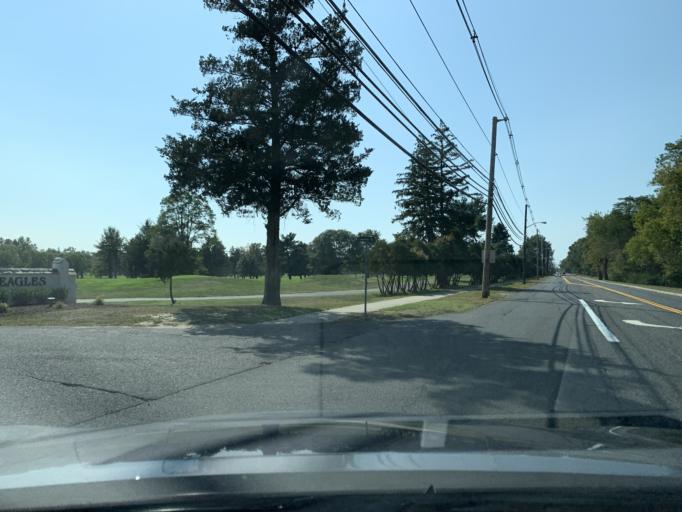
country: US
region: New Jersey
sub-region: Monmouth County
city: Eatontown
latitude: 40.3044
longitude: -74.0736
